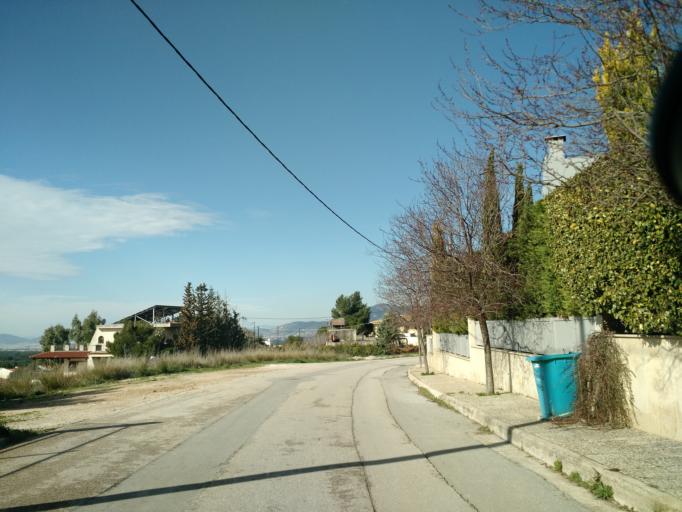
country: GR
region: Attica
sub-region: Nomarchia Anatolikis Attikis
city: Anoixi
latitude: 38.1331
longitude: 23.8678
